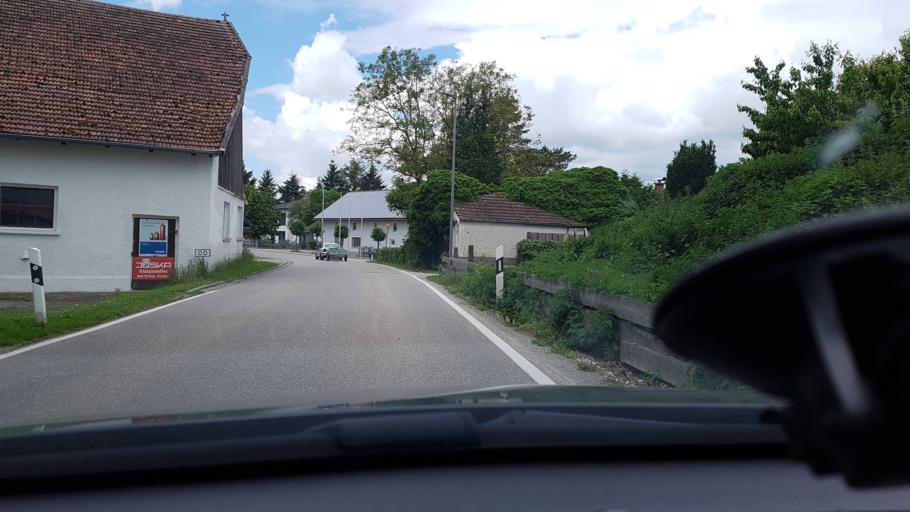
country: DE
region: Bavaria
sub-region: Lower Bavaria
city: Pocking
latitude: 48.4073
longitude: 13.3481
